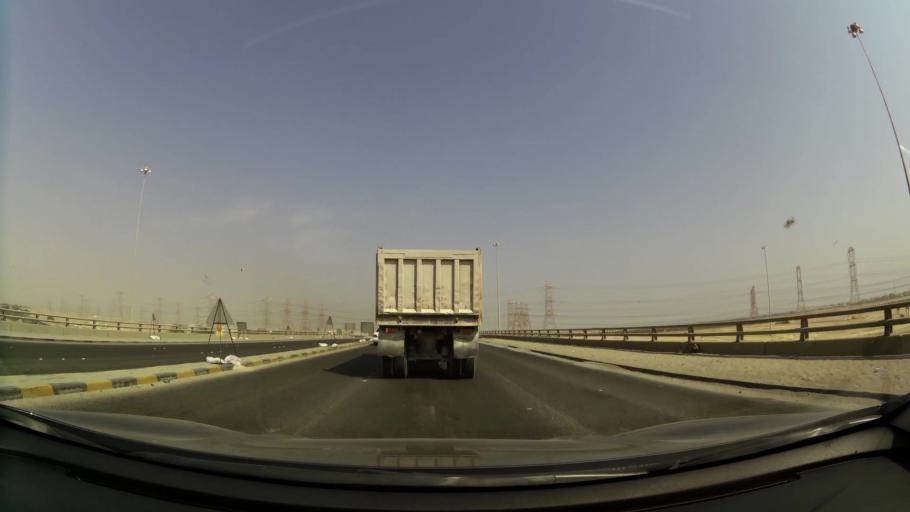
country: KW
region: Al Ahmadi
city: Al Fahahil
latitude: 28.9593
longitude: 48.1223
